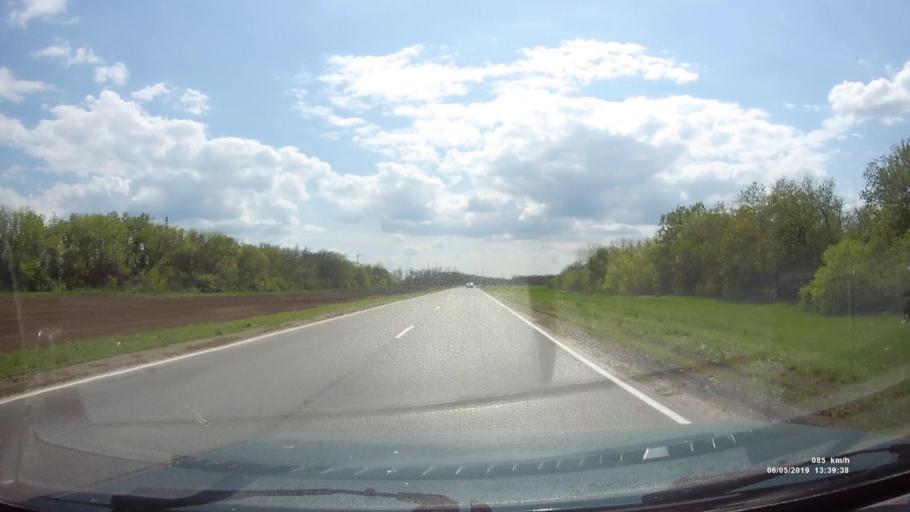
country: RU
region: Rostov
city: Ust'-Donetskiy
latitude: 47.6733
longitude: 40.7012
